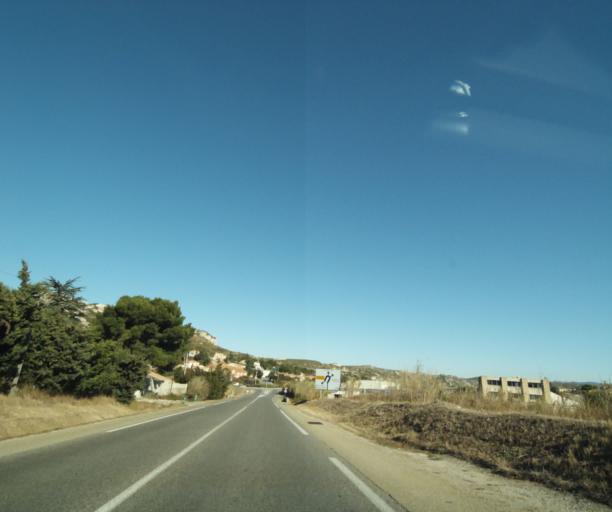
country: FR
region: Provence-Alpes-Cote d'Azur
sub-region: Departement des Bouches-du-Rhone
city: Le Rove
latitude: 43.3644
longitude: 5.2396
